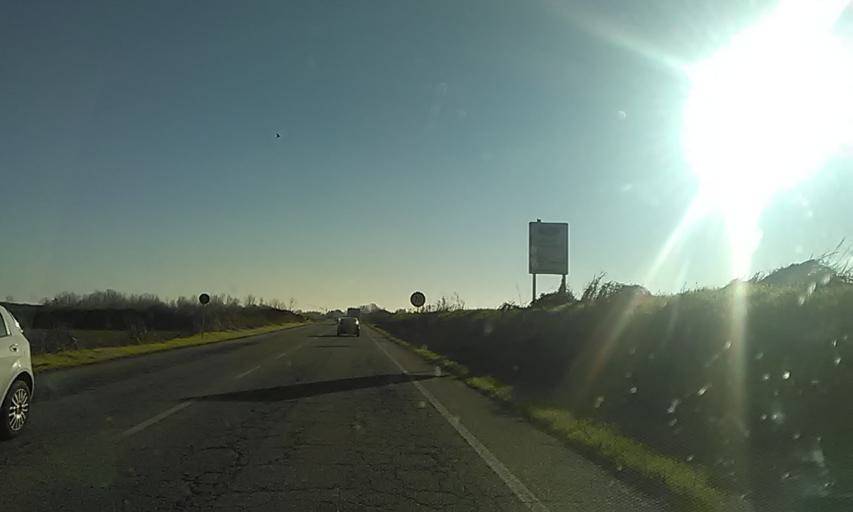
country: IT
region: Piedmont
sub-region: Provincia di Vercelli
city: Prarolo
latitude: 45.2681
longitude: 8.4637
